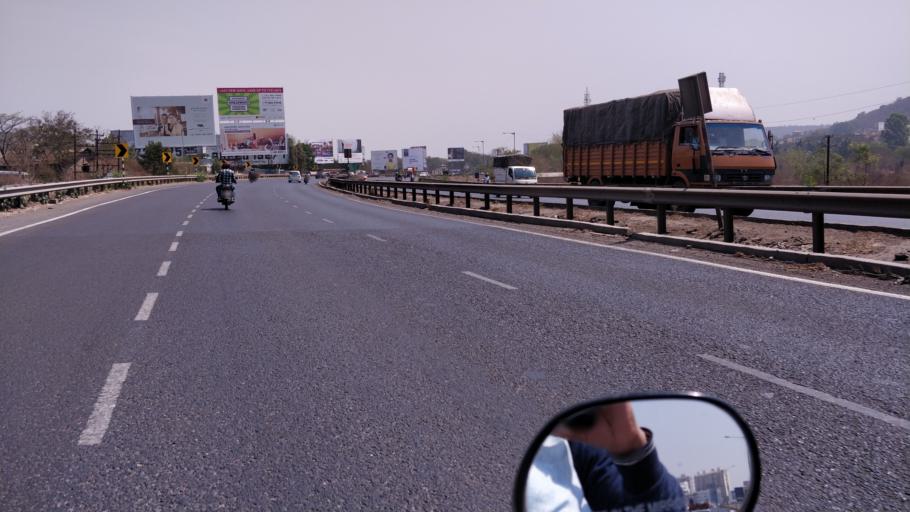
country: IN
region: Maharashtra
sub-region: Pune Division
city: Shivaji Nagar
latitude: 18.5250
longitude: 73.7719
